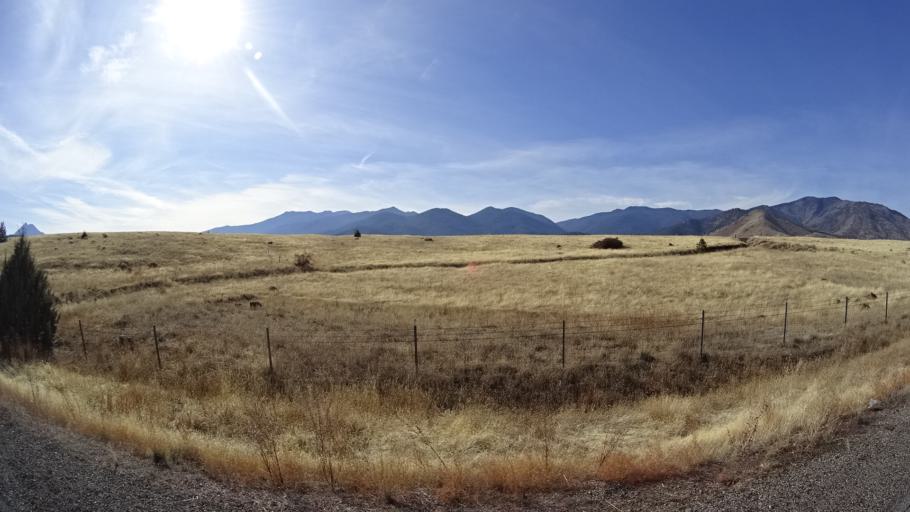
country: US
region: California
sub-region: Siskiyou County
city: Weed
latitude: 41.4711
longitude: -122.4446
